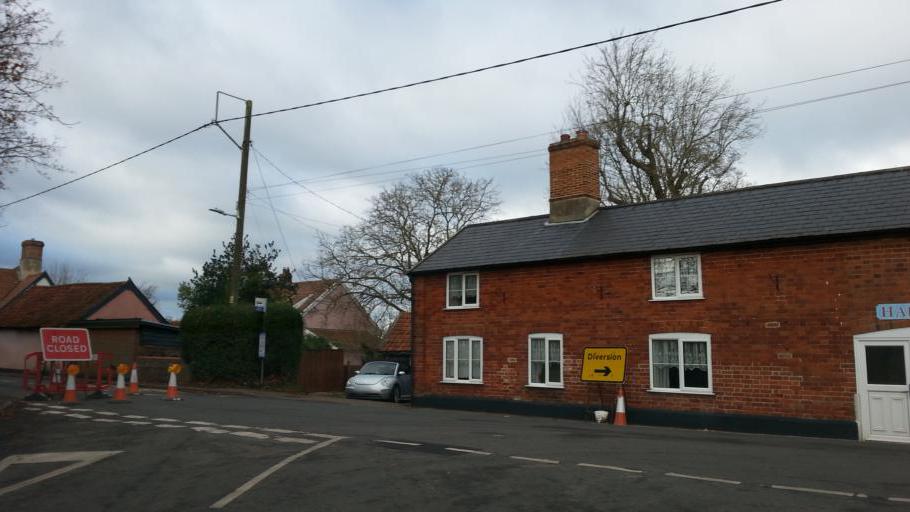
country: GB
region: England
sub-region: Suffolk
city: Ixworth
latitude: 52.3239
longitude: 0.8840
